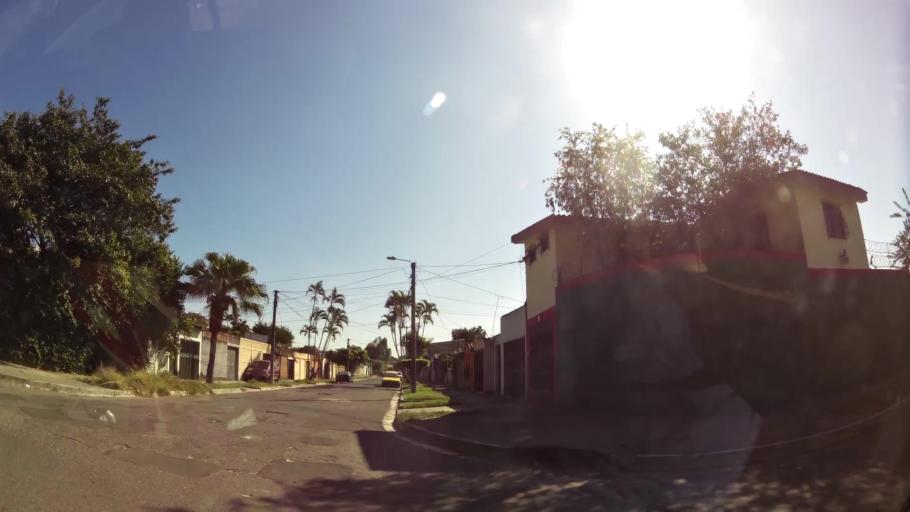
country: SV
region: La Libertad
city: Santa Tecla
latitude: 13.6785
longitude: -89.2956
